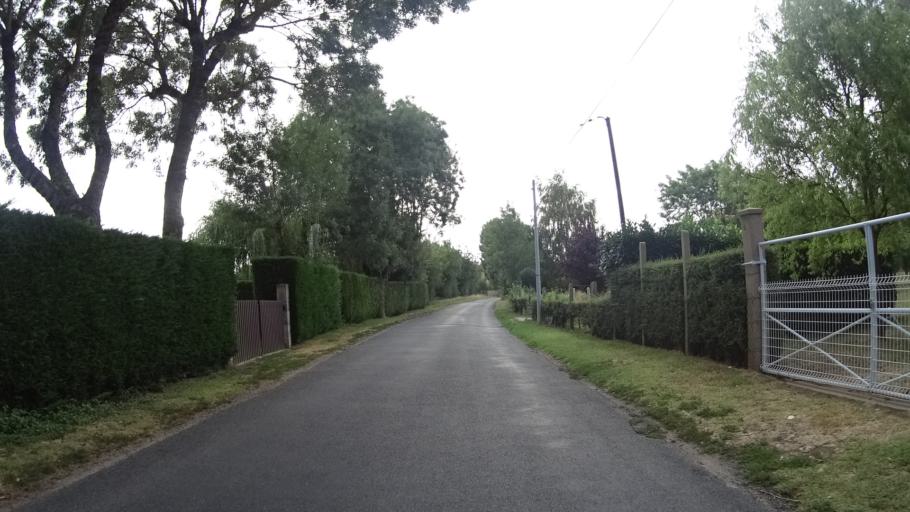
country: FR
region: Pays de la Loire
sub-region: Departement de la Loire-Atlantique
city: Anetz
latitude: 47.3657
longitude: -1.1141
